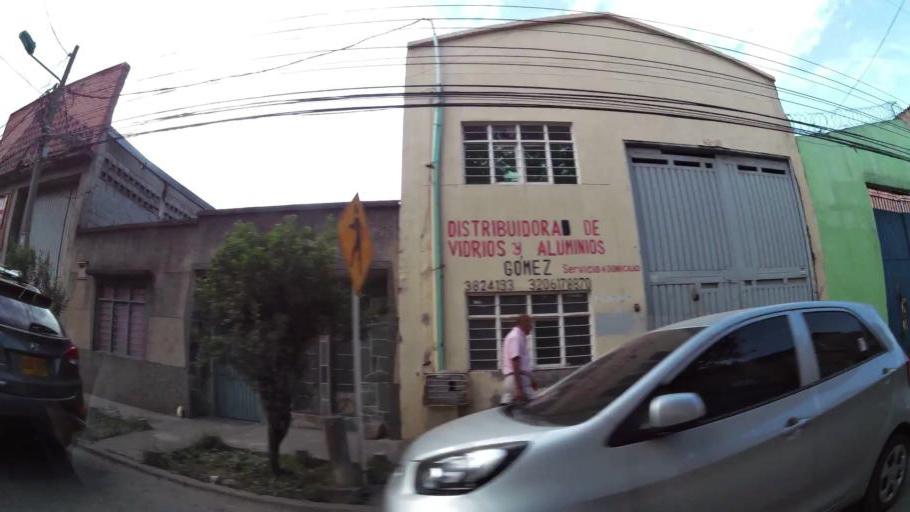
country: CO
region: Valle del Cauca
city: Cali
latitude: 3.4650
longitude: -76.5097
